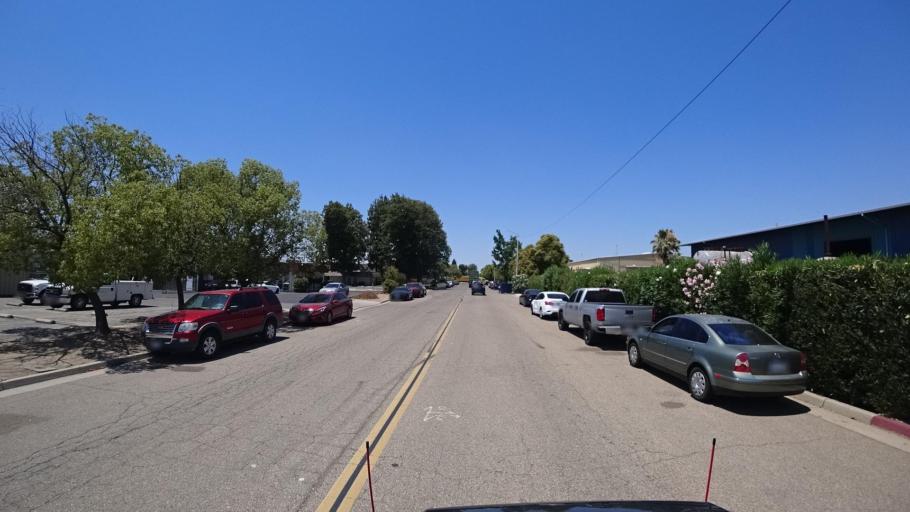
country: US
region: California
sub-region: Fresno County
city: Sunnyside
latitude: 36.7618
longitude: -119.7160
